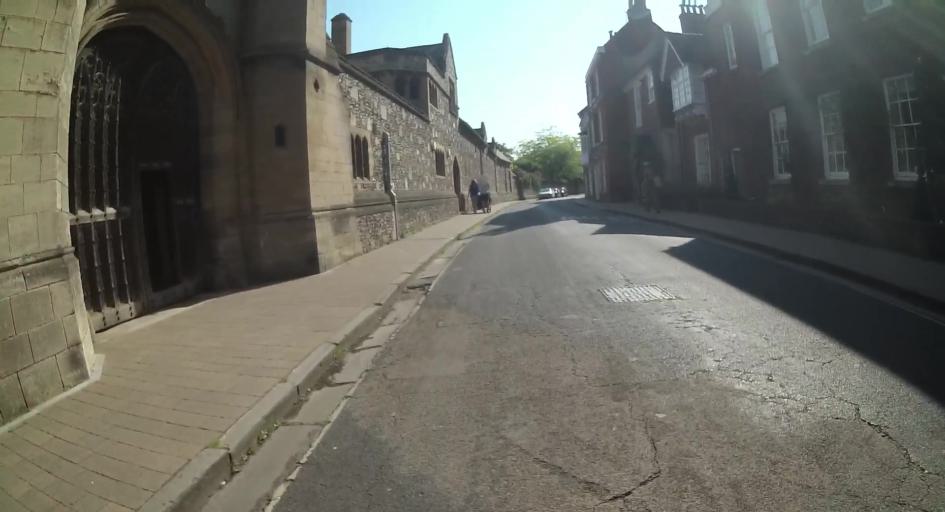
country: GB
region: England
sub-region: Hampshire
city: Winchester
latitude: 51.0574
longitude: -1.3153
